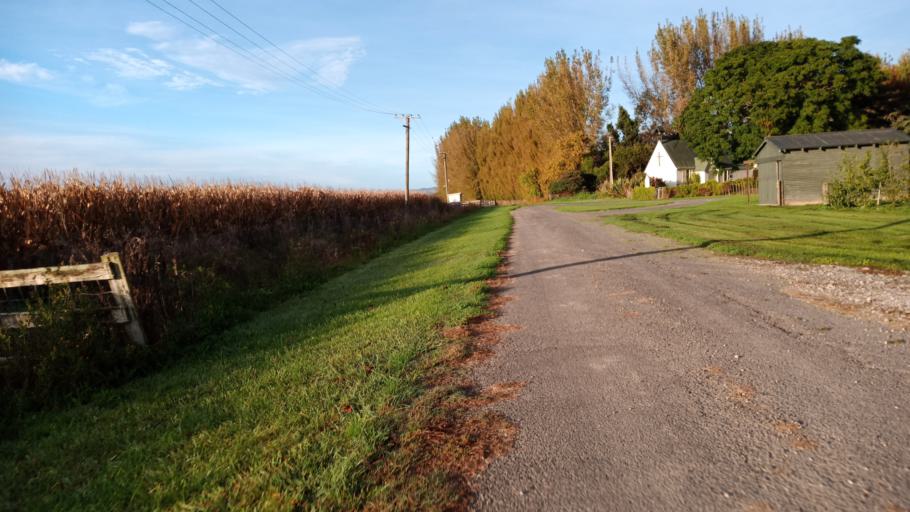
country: NZ
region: Gisborne
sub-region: Gisborne District
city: Gisborne
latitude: -38.6535
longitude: 177.9417
